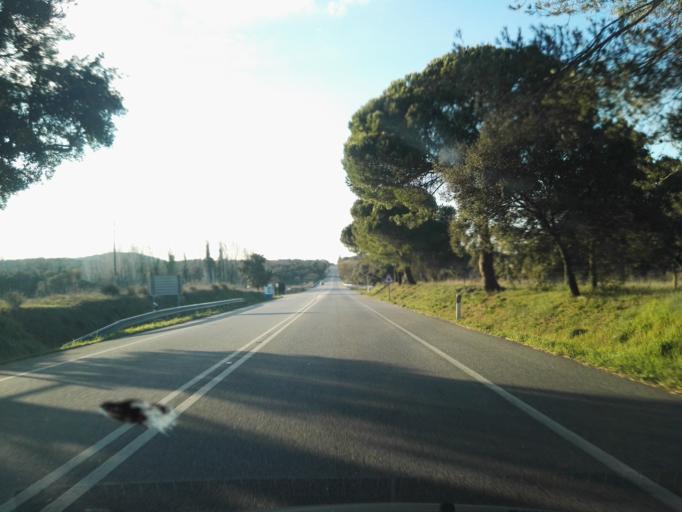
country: PT
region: Evora
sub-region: Montemor-O-Novo
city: Montemor-o-Novo
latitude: 38.6181
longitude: -8.0841
